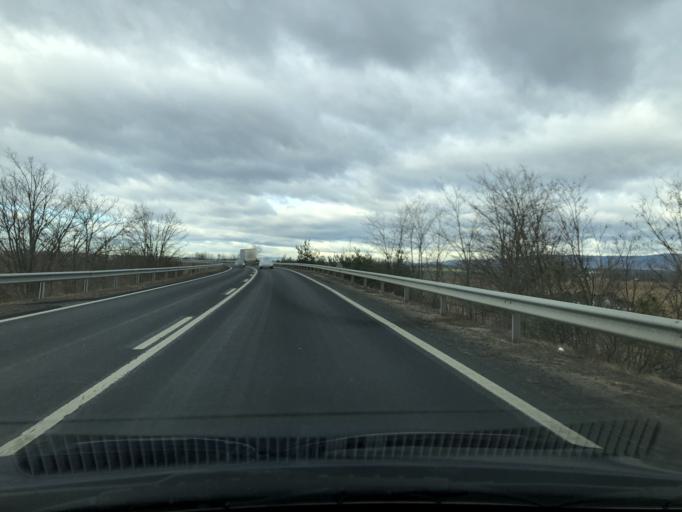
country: HU
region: Vas
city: Gencsapati
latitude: 47.2501
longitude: 16.5557
